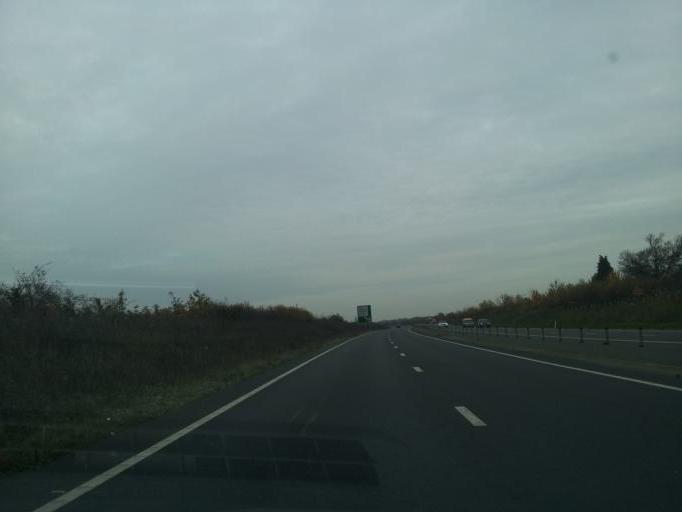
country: GB
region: England
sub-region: Cambridgeshire
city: Comberton
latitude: 52.2199
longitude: -0.0204
